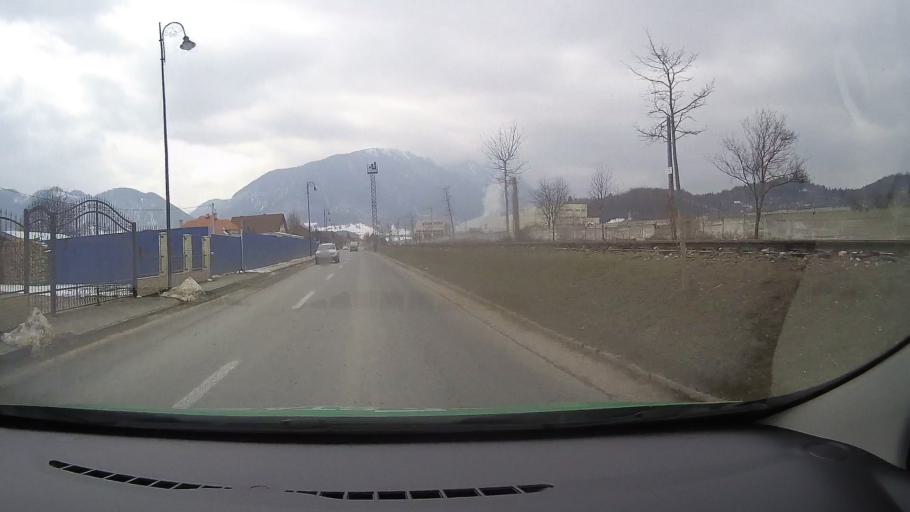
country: RO
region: Brasov
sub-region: Comuna Zarnesti
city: Zarnesti
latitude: 45.5645
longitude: 25.3357
